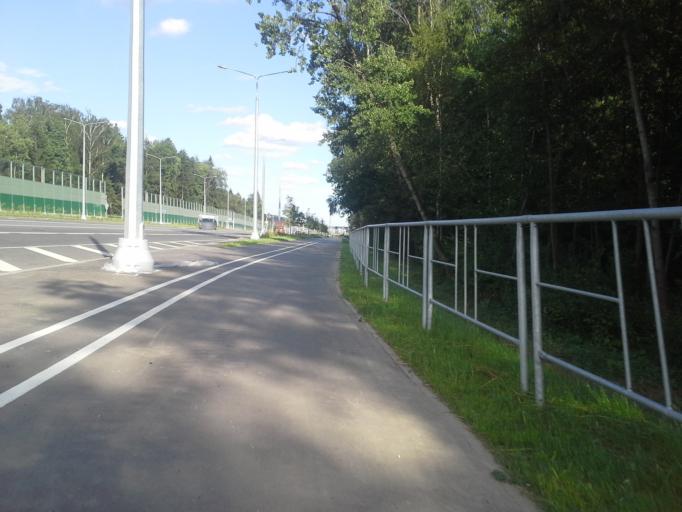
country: RU
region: Moscow
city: Vnukovo
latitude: 55.5344
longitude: 37.2086
